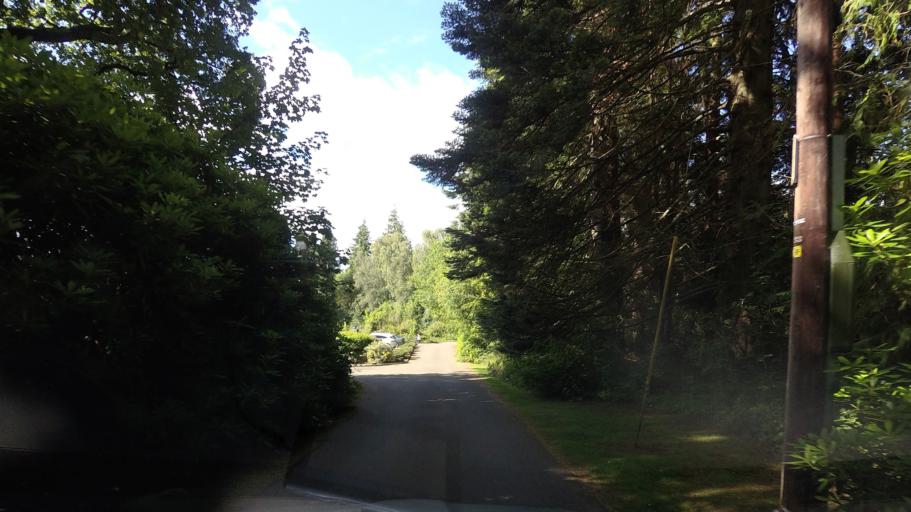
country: GB
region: Scotland
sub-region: Stirling
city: Killearn
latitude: 56.0685
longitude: -4.4797
